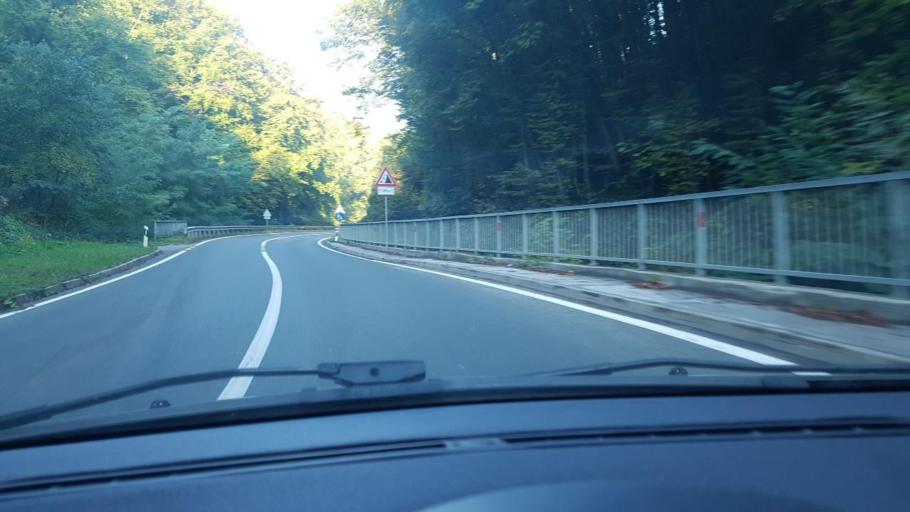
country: HR
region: Krapinsko-Zagorska
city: Marija Bistrica
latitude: 45.9458
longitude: 16.0987
